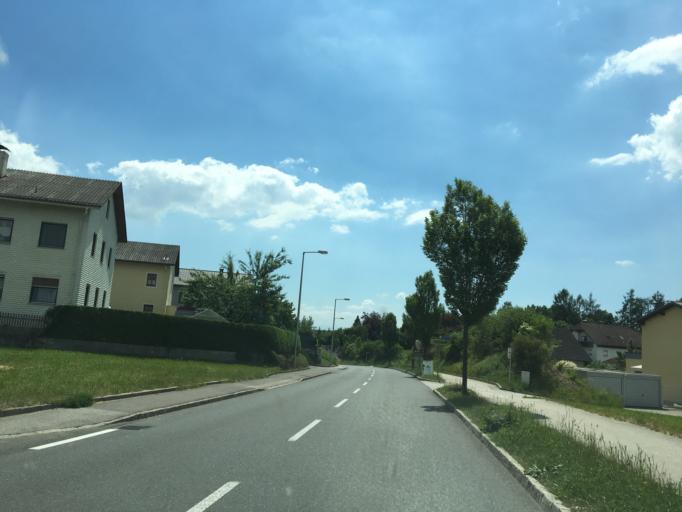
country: AT
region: Upper Austria
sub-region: Politischer Bezirk Urfahr-Umgebung
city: Engerwitzdorf
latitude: 48.3620
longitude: 14.5339
